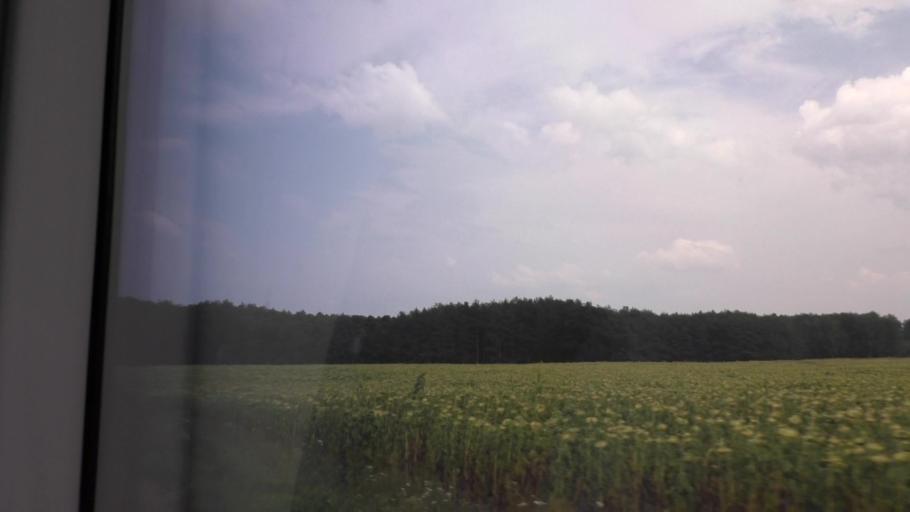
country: DE
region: Brandenburg
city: Mixdorf
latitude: 52.1932
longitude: 14.3917
